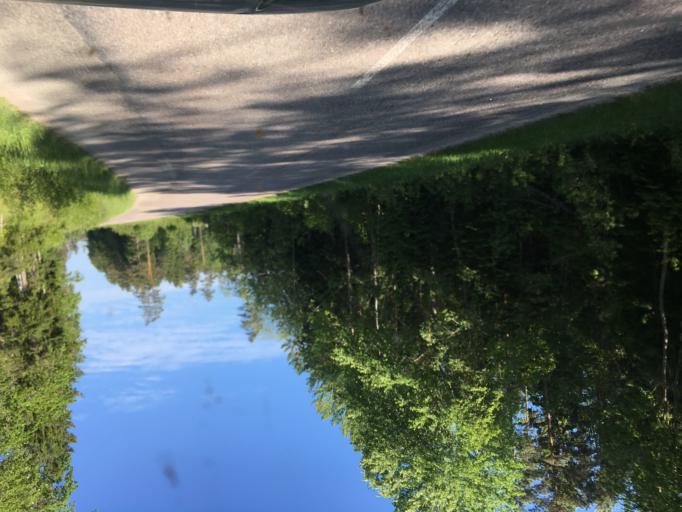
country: LV
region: Ventspils
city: Ventspils
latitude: 57.4921
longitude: 21.8064
